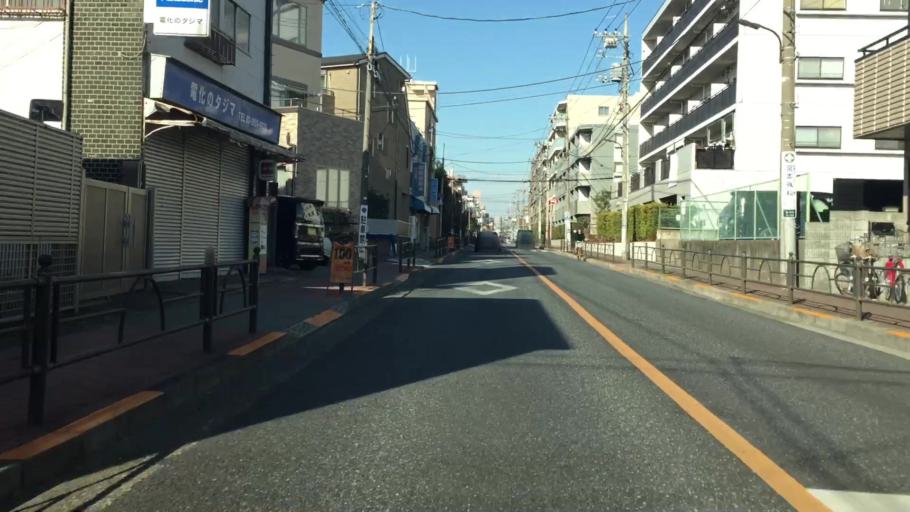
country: JP
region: Saitama
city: Wako
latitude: 35.7550
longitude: 139.6670
